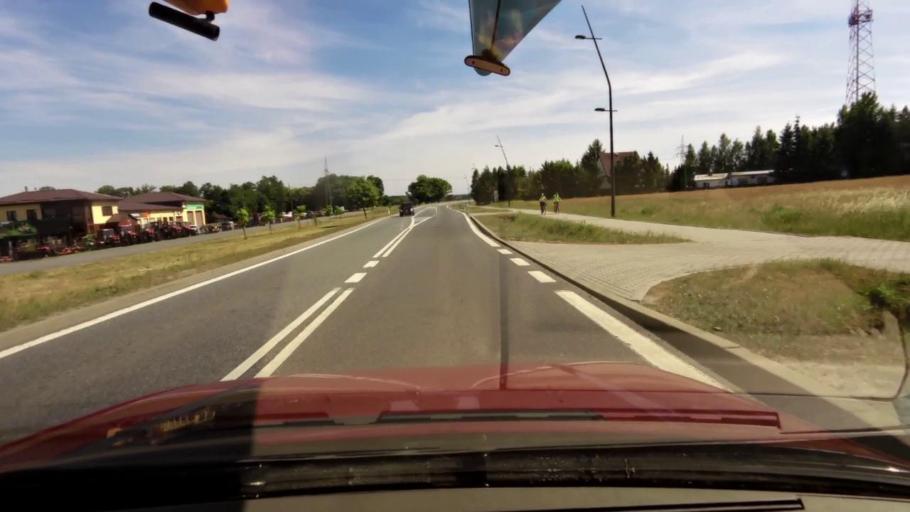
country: PL
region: Pomeranian Voivodeship
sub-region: Powiat slupski
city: Kobylnica
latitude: 54.4304
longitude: 17.0048
